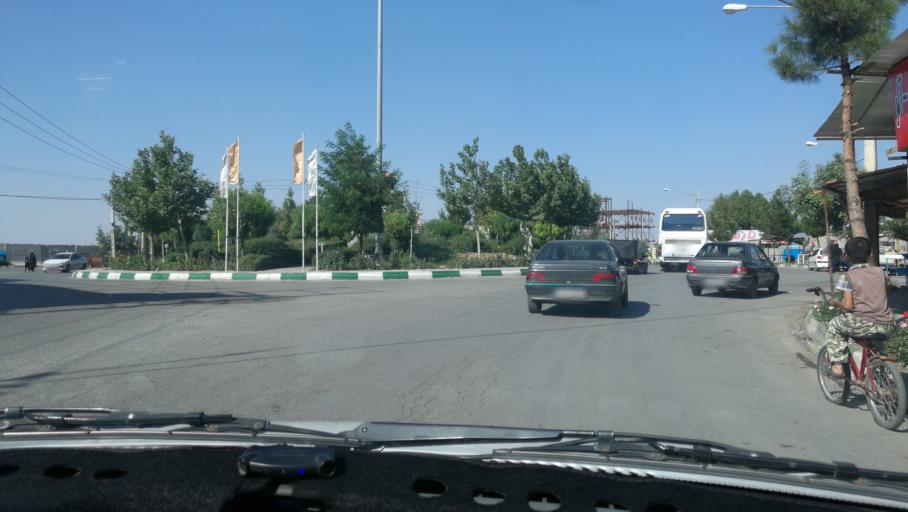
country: IR
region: Razavi Khorasan
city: Torqabeh
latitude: 36.3891
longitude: 59.2675
